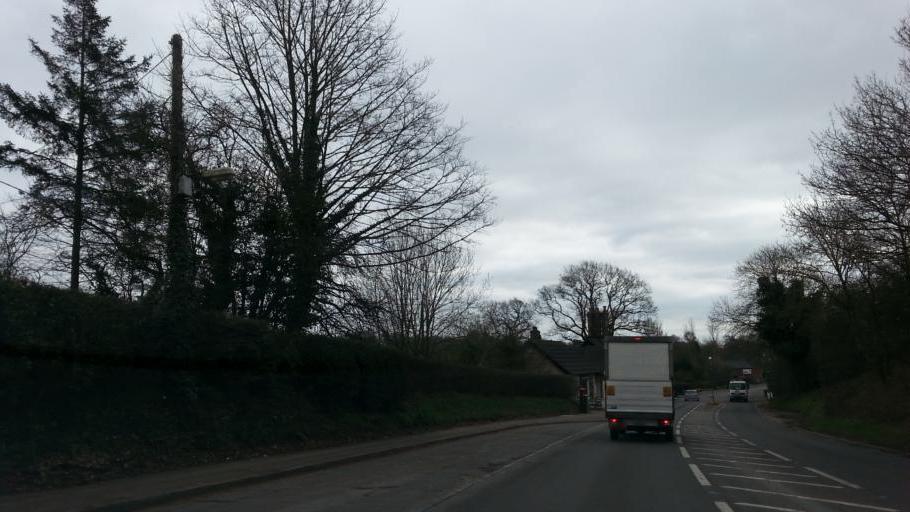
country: GB
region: England
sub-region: Staffordshire
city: Stafford
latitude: 52.8656
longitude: -2.0805
